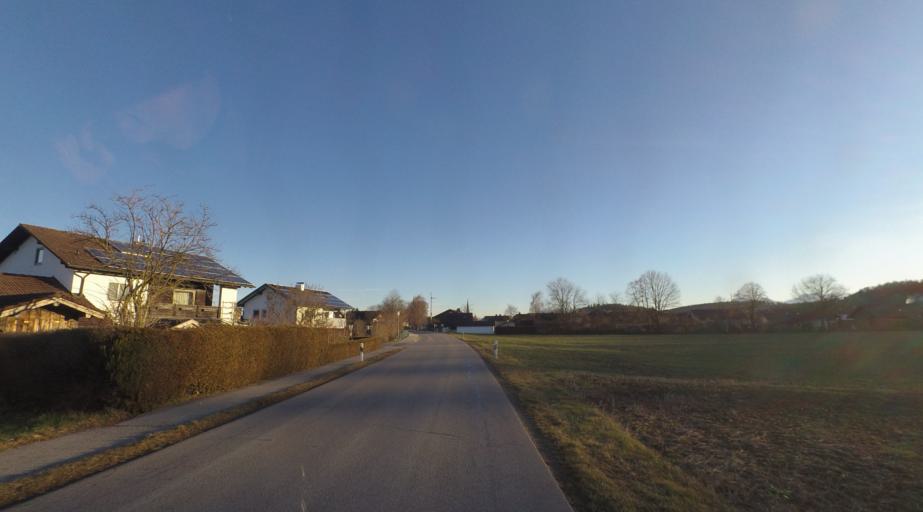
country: DE
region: Bavaria
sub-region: Upper Bavaria
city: Kirchanschoring
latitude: 47.9574
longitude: 12.8303
